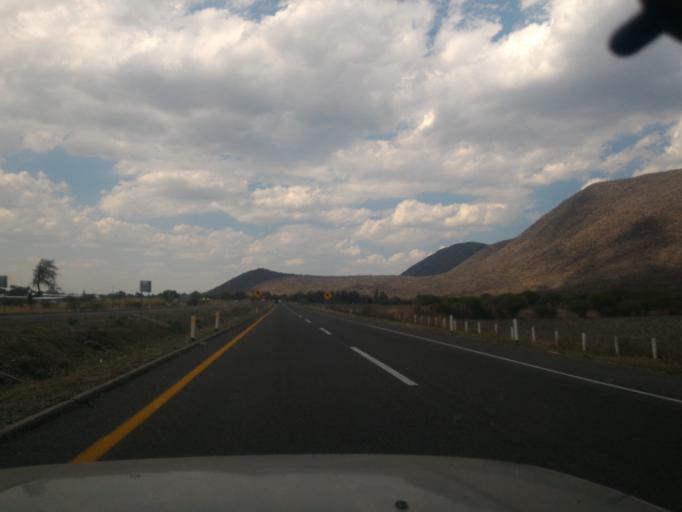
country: MX
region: Jalisco
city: Zacoalco de Torres
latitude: 20.1791
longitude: -103.5109
